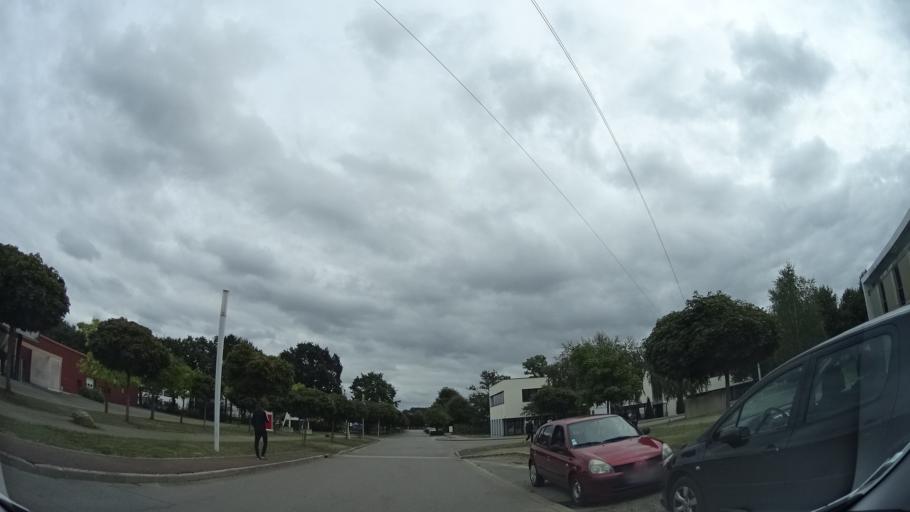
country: FR
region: Brittany
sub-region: Departement d'Ille-et-Vilaine
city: Bruz
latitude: 48.0497
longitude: -1.7435
